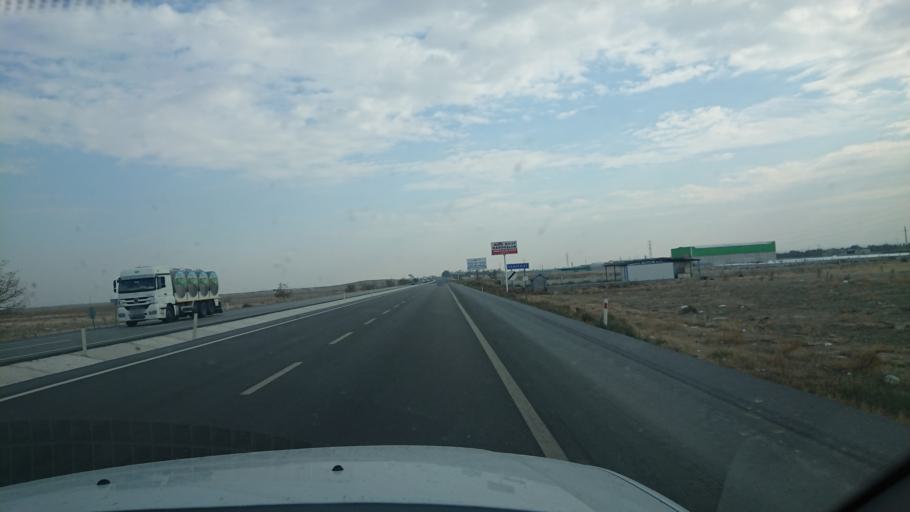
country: TR
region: Aksaray
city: Yesilova
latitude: 38.2933
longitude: 33.7696
